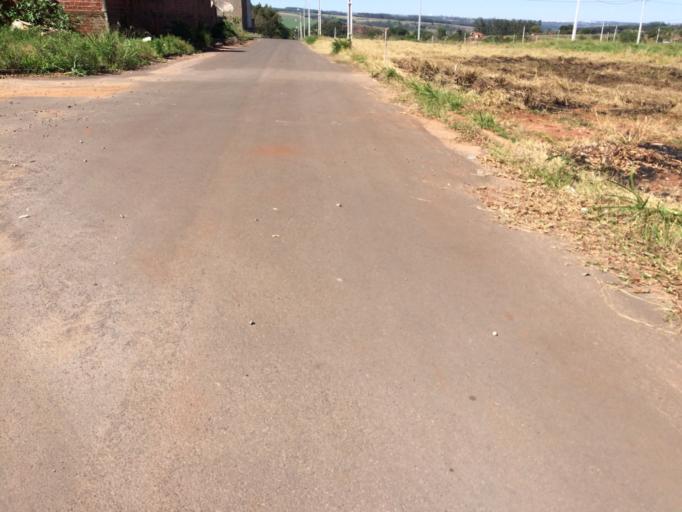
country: BR
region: Parana
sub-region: Cianorte
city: Cianorte
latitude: -23.5392
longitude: -52.5946
